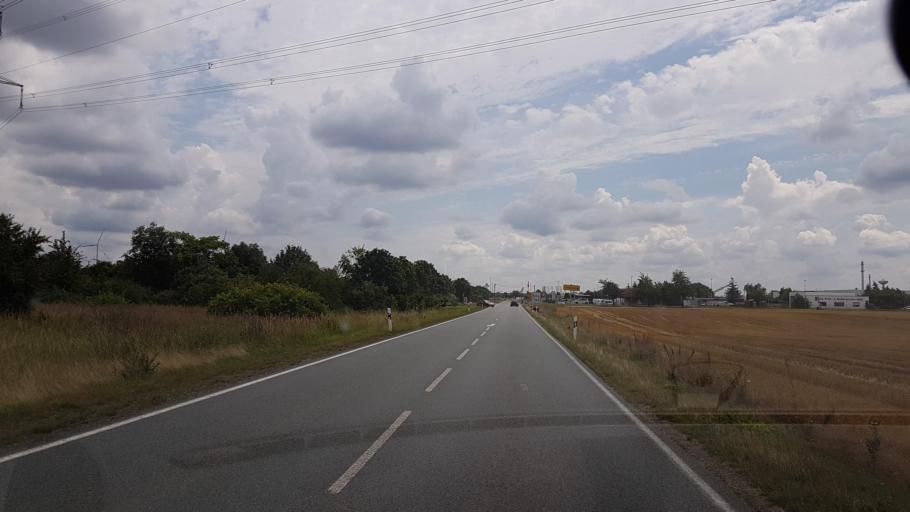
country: DE
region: Saxony
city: Zeithain
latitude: 51.3426
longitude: 13.3400
